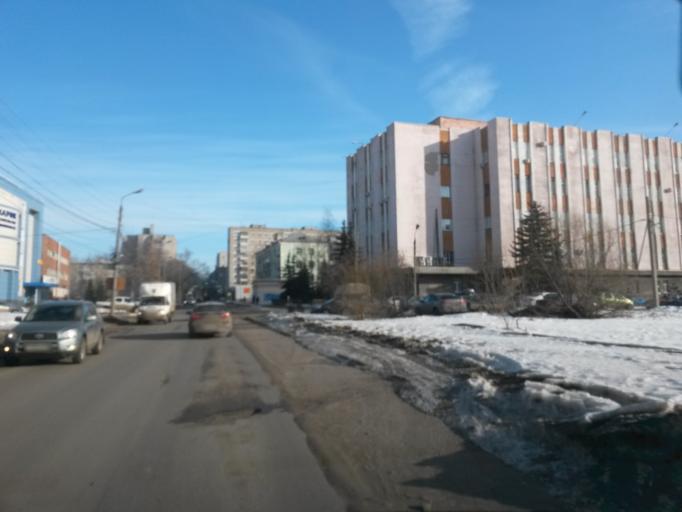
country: RU
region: Jaroslavl
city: Yaroslavl
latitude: 57.6189
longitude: 39.8534
